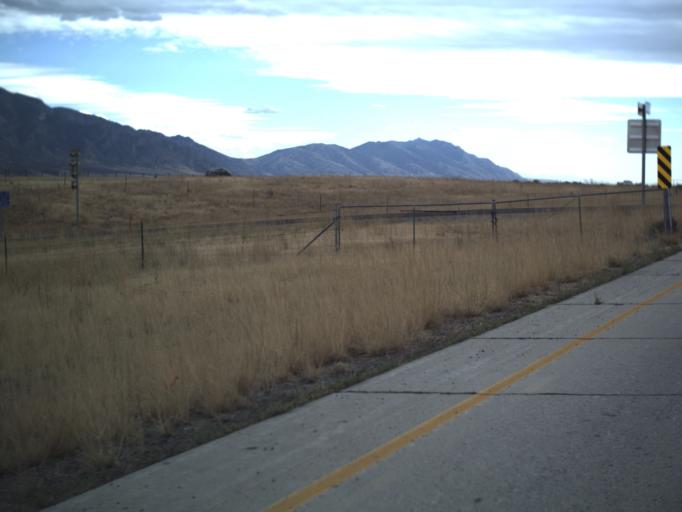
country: US
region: Utah
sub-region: Box Elder County
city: Garland
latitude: 41.7851
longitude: -112.1740
